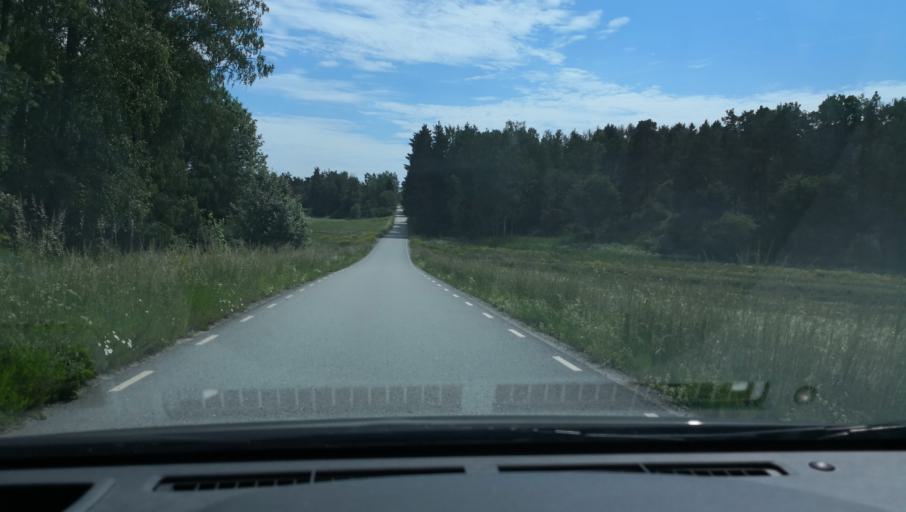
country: SE
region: Uppsala
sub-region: Habo Kommun
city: Balsta
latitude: 59.6837
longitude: 17.4638
